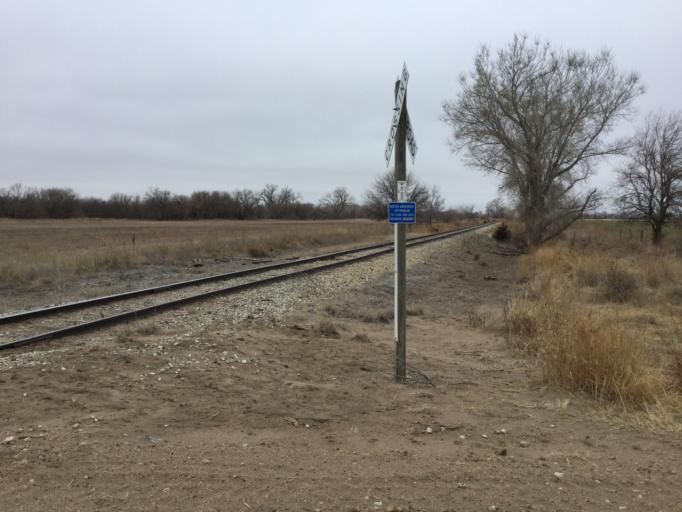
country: US
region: Kansas
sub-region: Barton County
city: Ellinwood
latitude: 38.3104
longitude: -98.4796
